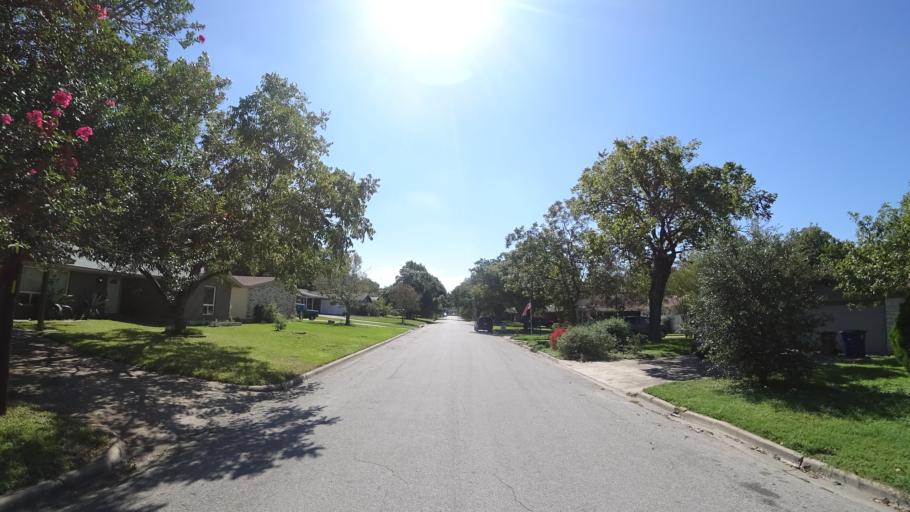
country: US
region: Texas
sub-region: Travis County
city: Austin
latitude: 30.3096
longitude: -97.6928
